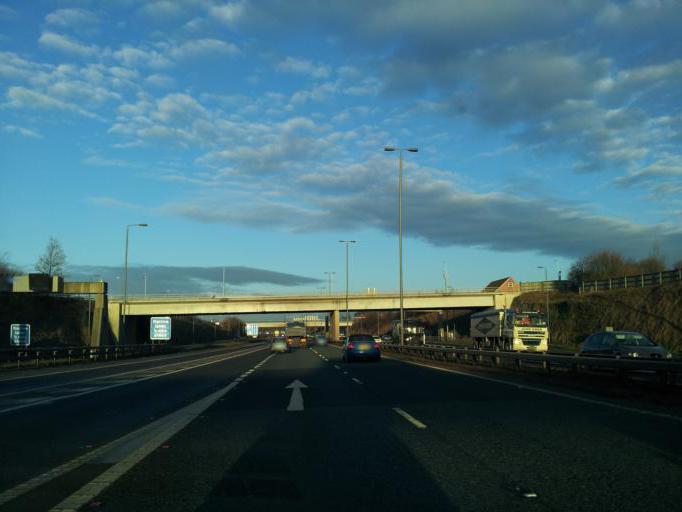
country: GB
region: England
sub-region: City and Borough of Leeds
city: Lofthouse
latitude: 53.7325
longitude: -1.5203
